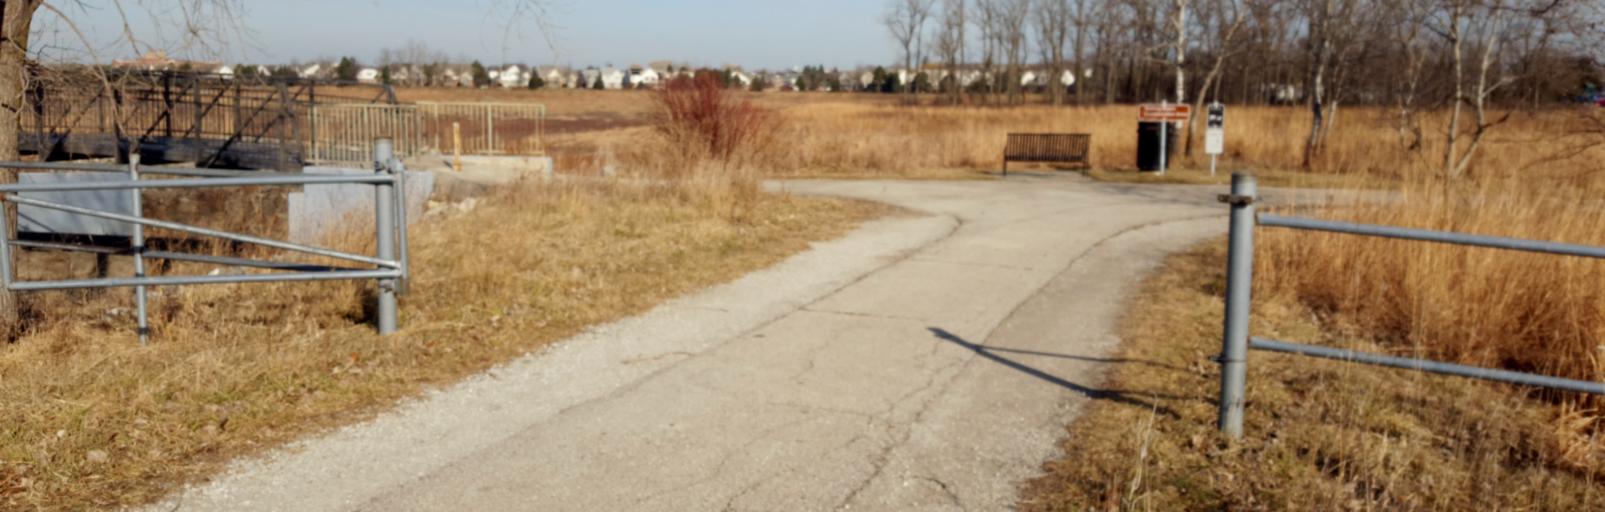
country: US
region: Illinois
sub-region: Cook County
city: Northfield
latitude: 42.0974
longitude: -87.8086
